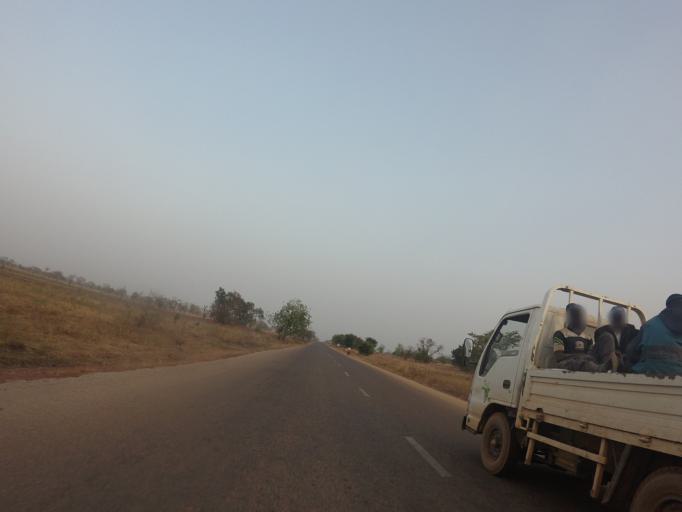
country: GH
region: Northern
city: Tamale
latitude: 9.4405
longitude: -1.1008
